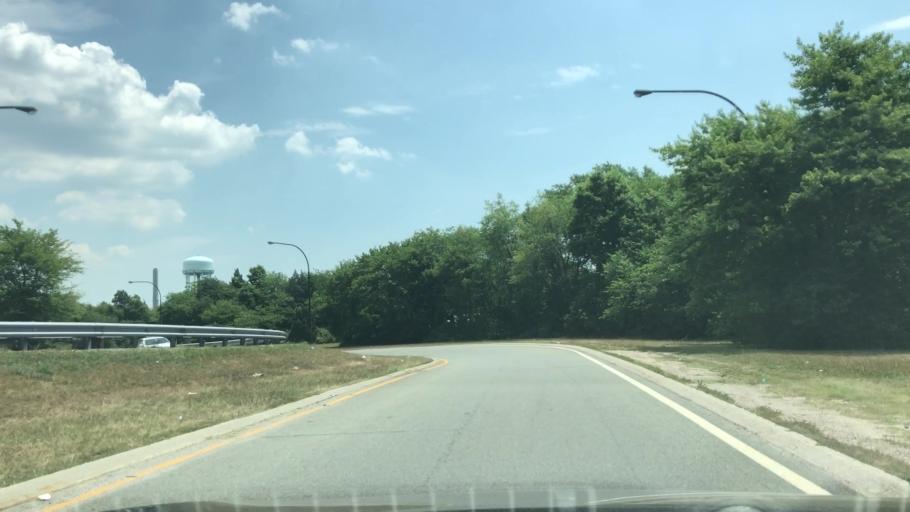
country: US
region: New York
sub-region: Nassau County
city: East Garden City
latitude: 40.7365
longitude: -73.6082
